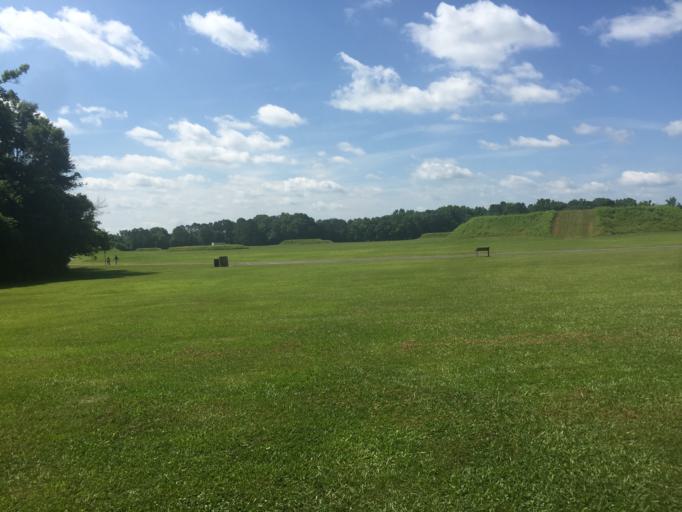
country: US
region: Alabama
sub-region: Hale County
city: Moundville
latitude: 33.0078
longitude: -87.6307
